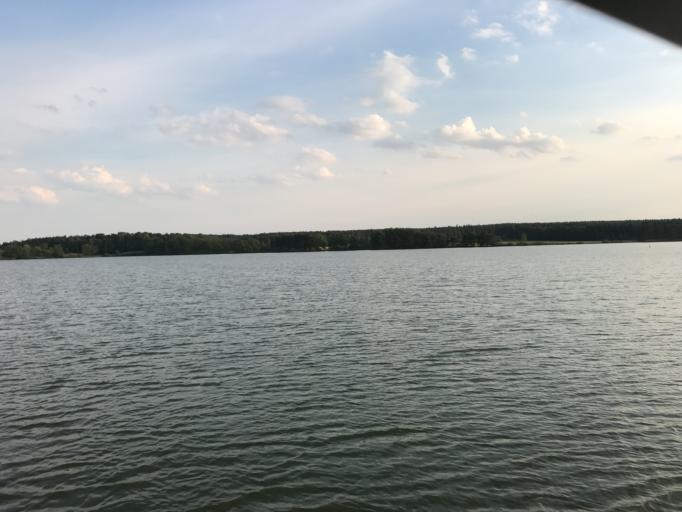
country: CZ
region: Jihocesky
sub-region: Okres Jindrichuv Hradec
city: Trebon
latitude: 48.9952
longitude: 14.7425
